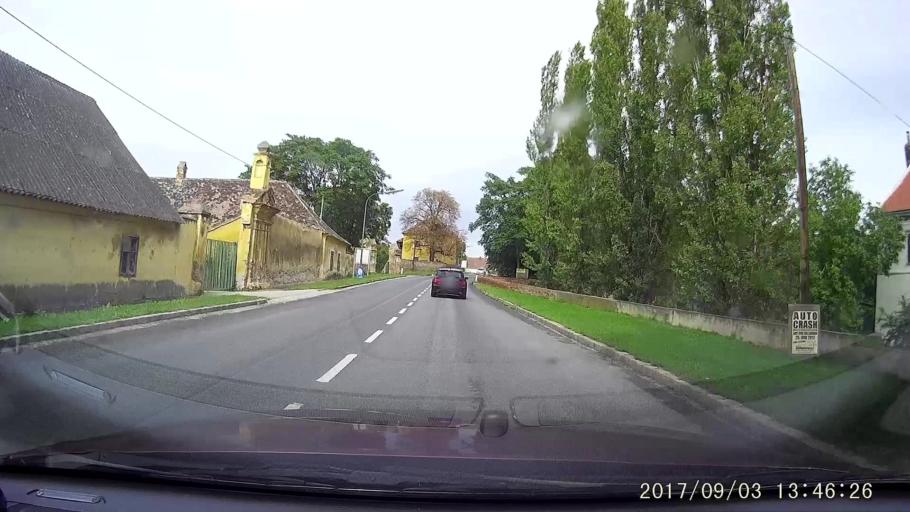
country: AT
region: Lower Austria
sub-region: Politischer Bezirk Hollabrunn
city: Guntersdorf
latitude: 48.6499
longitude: 16.0496
